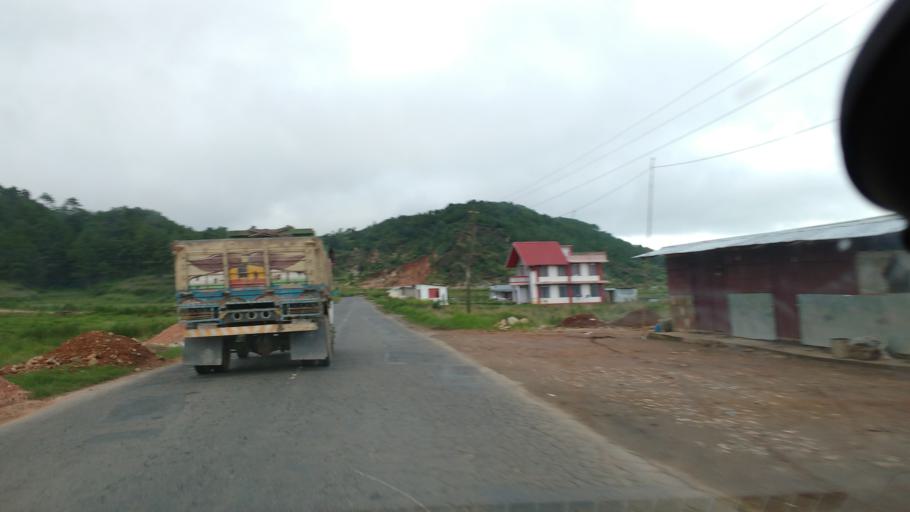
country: IN
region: Meghalaya
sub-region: East Khasi Hills
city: Shillong
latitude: 25.5217
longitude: 91.8157
